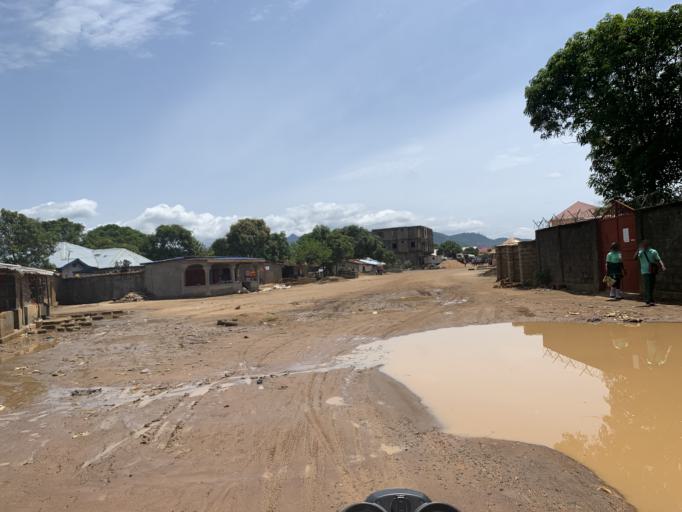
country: SL
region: Western Area
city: Waterloo
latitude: 8.3353
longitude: -13.0404
